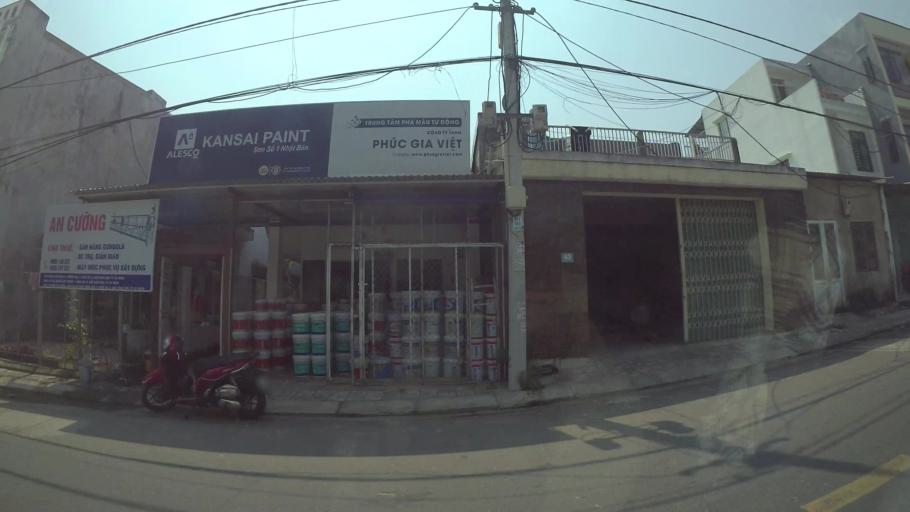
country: VN
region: Da Nang
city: Ngu Hanh Son
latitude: 16.0235
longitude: 108.2477
